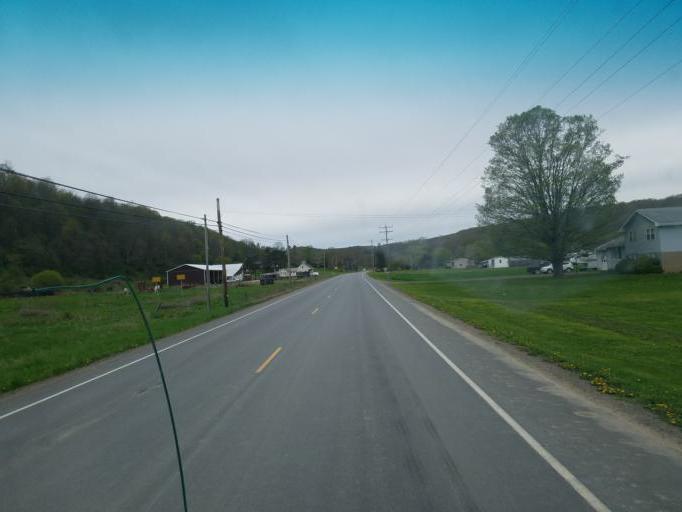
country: US
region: Pennsylvania
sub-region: Tioga County
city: Westfield
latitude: 41.9246
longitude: -77.6262
